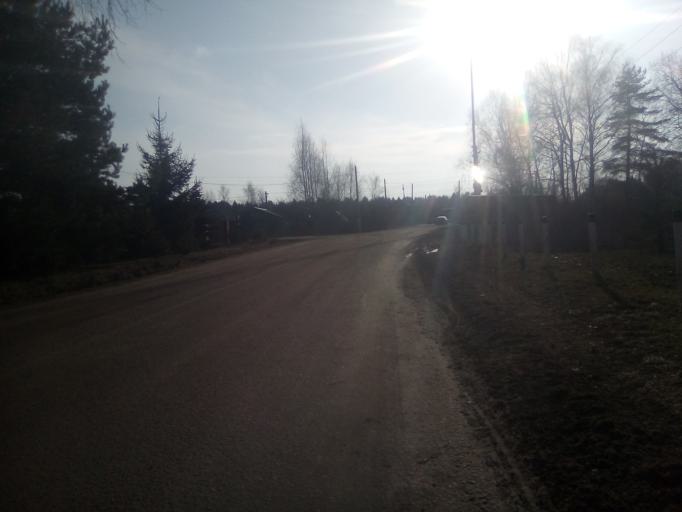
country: RU
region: Moscow
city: Tolstopal'tsevo
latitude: 55.6247
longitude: 37.2215
